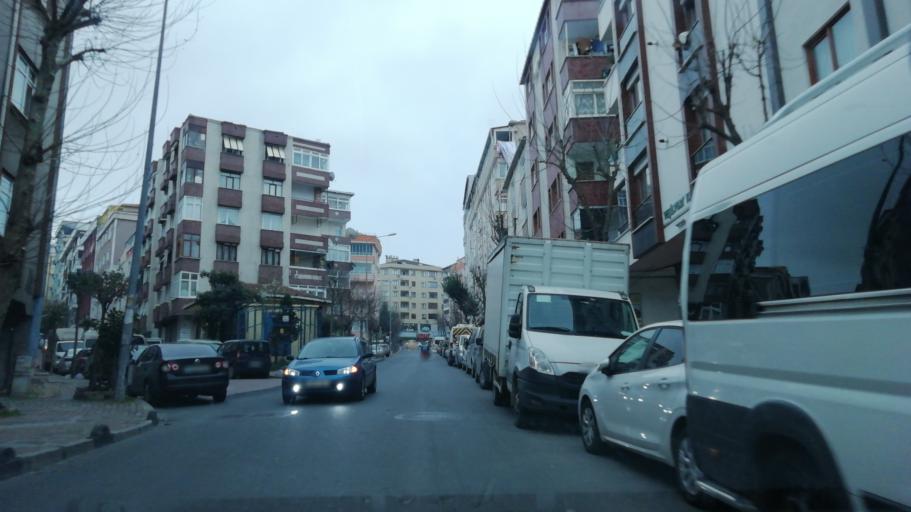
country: TR
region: Istanbul
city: Bahcelievler
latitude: 41.0055
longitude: 28.8505
